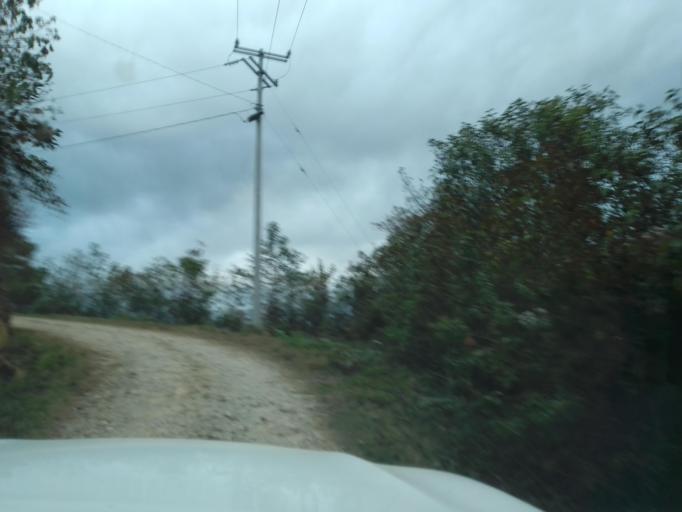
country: MX
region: Chiapas
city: Motozintla de Mendoza
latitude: 15.2118
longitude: -92.2276
